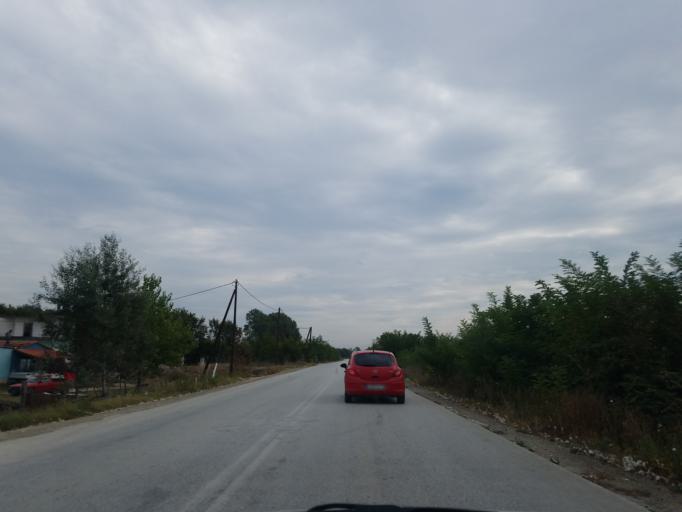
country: GR
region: Thessaly
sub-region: Nomos Kardhitsas
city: Sofades
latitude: 39.3248
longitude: 22.1006
